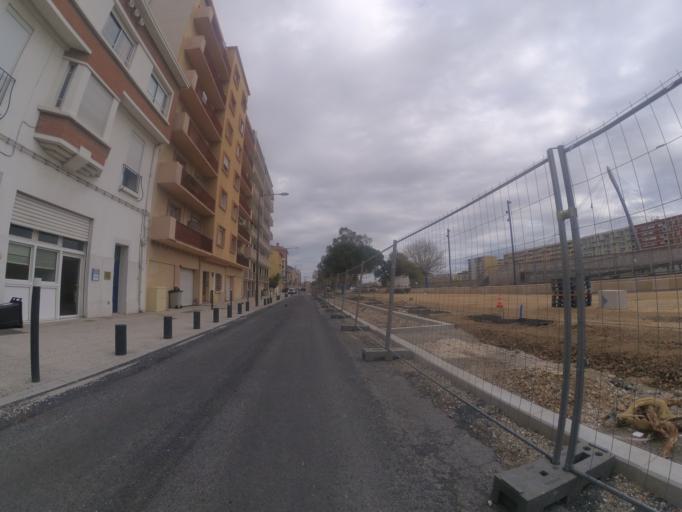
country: FR
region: Languedoc-Roussillon
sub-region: Departement des Pyrenees-Orientales
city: Perpignan
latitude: 42.7034
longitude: 2.8878
